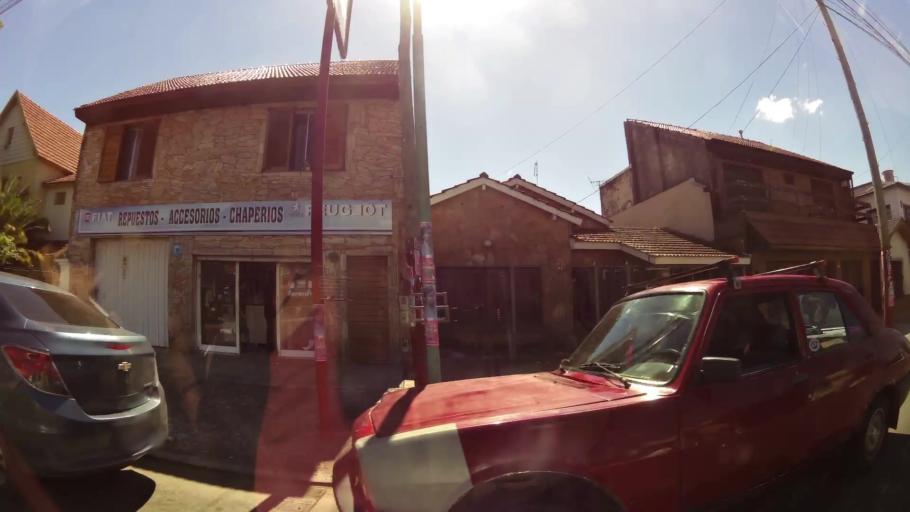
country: AR
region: Buenos Aires
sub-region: Partido de Lomas de Zamora
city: Lomas de Zamora
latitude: -34.7570
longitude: -58.4215
